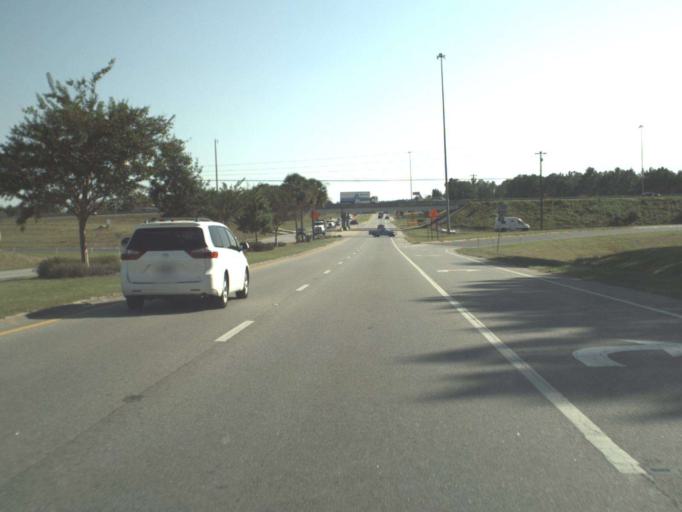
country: US
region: Florida
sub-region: Walton County
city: DeFuniak Springs
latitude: 30.6947
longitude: -86.1226
